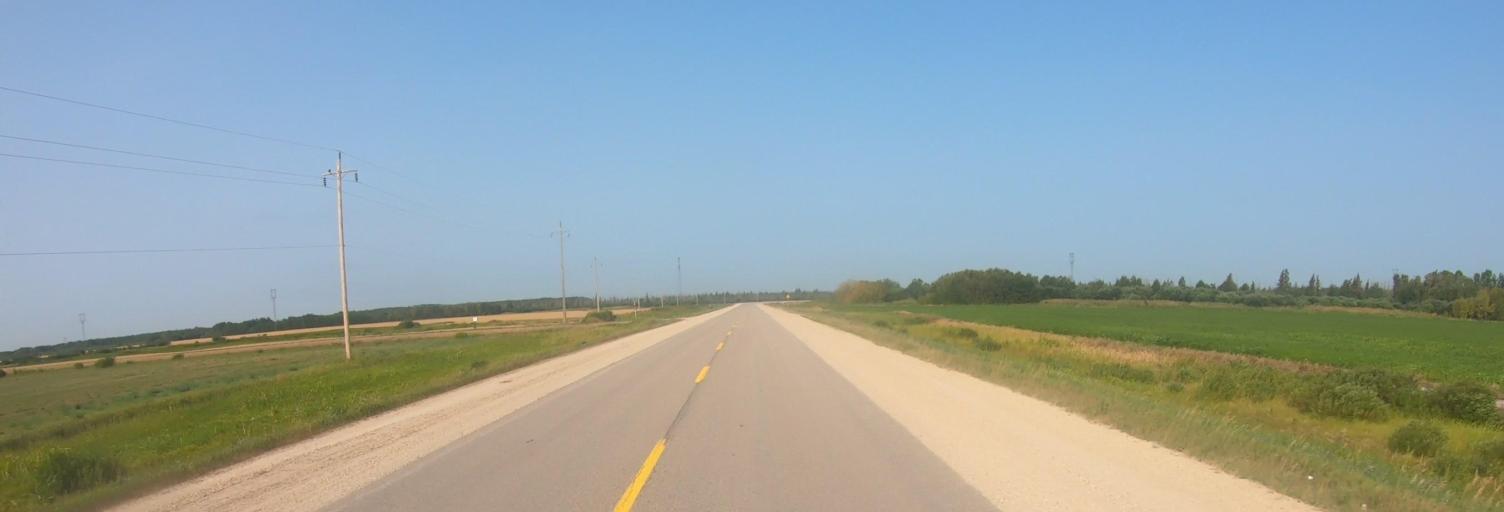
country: US
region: Minnesota
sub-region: Roseau County
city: Warroad
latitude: 49.0159
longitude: -95.5293
